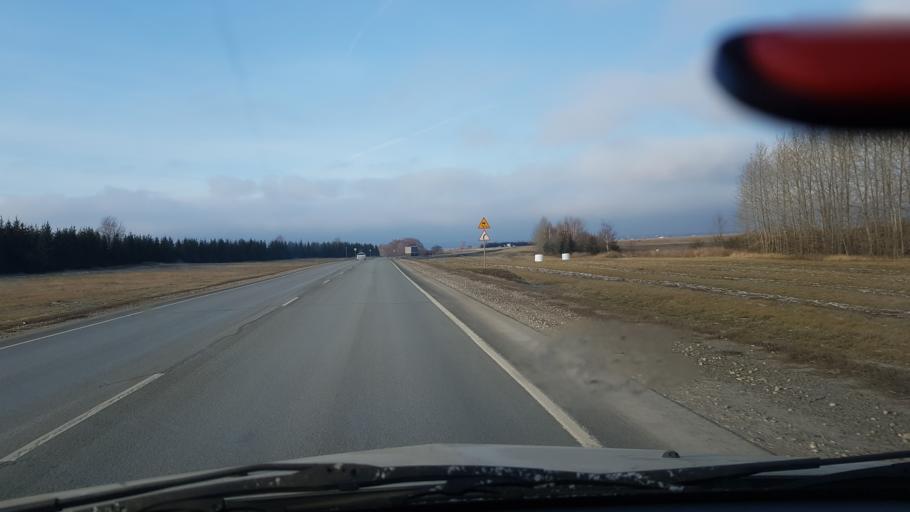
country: RU
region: Tatarstan
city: Laishevo
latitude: 55.3972
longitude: 49.7724
